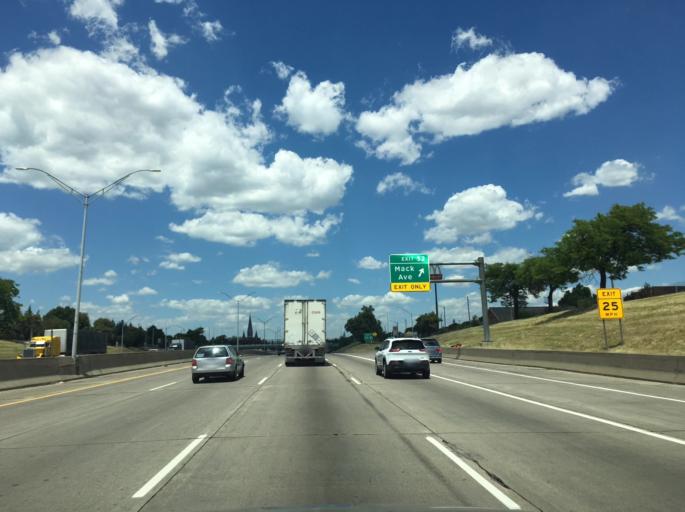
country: US
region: Michigan
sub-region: Wayne County
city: Detroit
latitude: 42.3487
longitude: -83.0461
